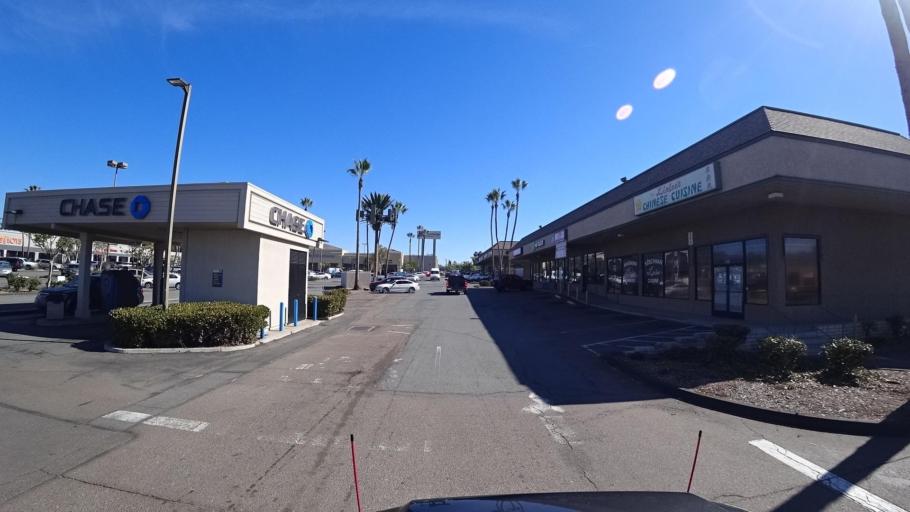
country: US
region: California
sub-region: San Diego County
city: La Presa
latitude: 32.7073
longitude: -117.0102
